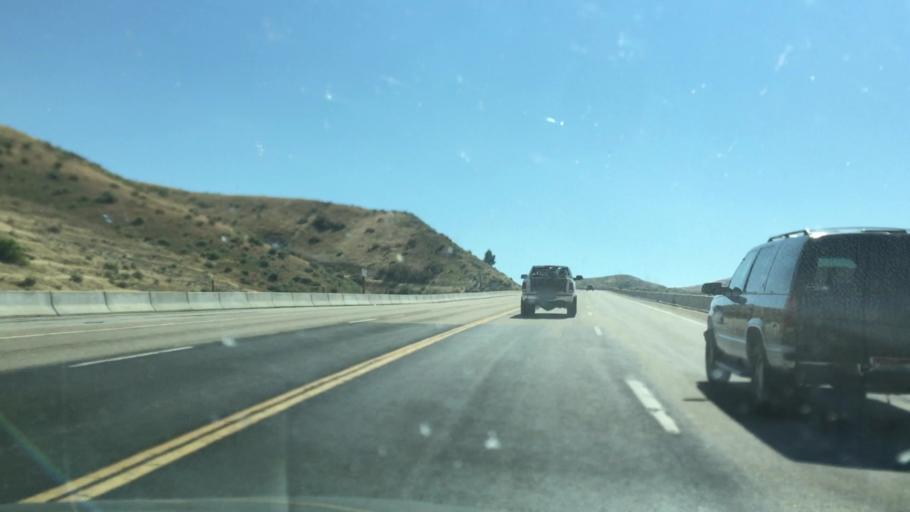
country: US
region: Idaho
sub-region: Ada County
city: Eagle
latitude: 43.8453
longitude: -116.2300
